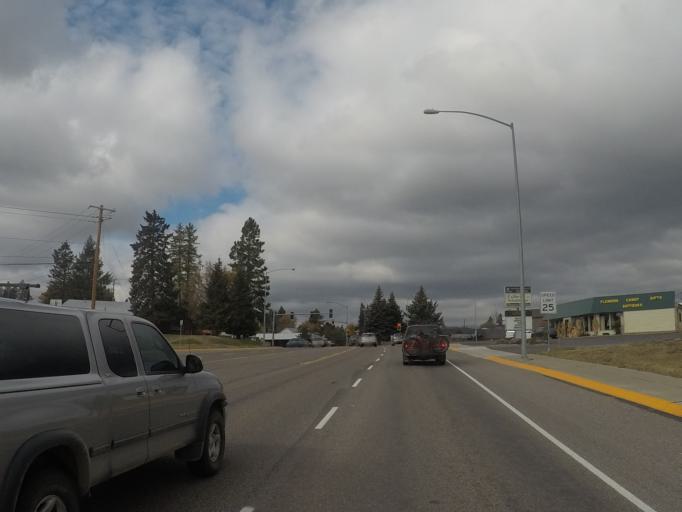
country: US
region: Montana
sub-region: Flathead County
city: Columbia Falls
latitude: 48.3689
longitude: -114.1798
